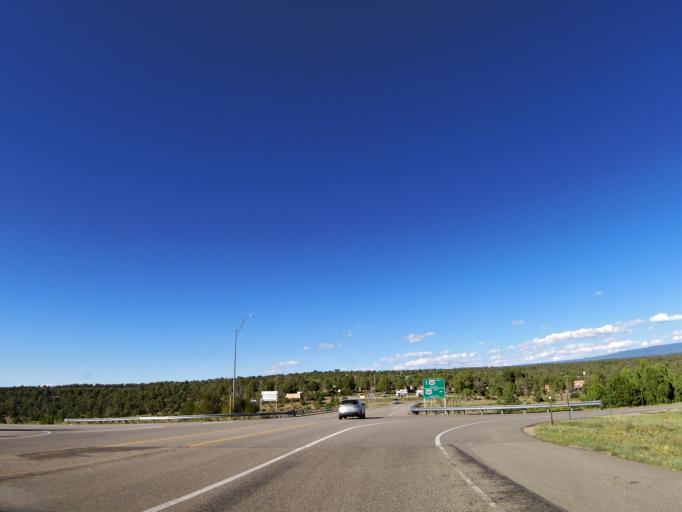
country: US
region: Colorado
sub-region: Montezuma County
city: Mancos
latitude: 37.3398
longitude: -108.4119
